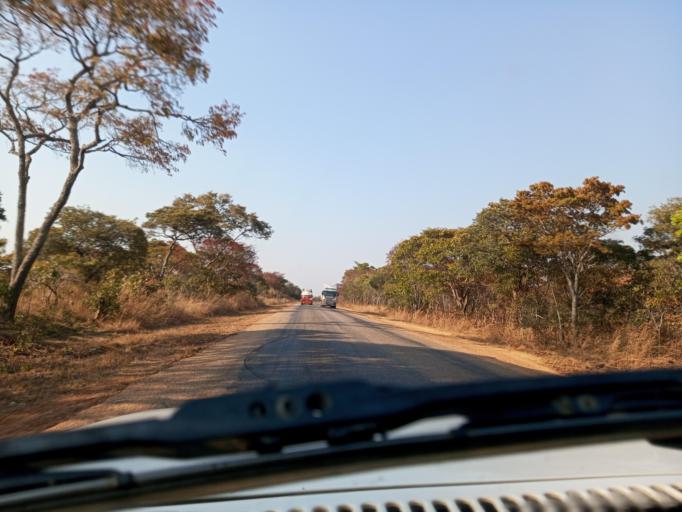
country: ZM
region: Northern
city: Mpika
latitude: -12.3628
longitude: 31.1041
